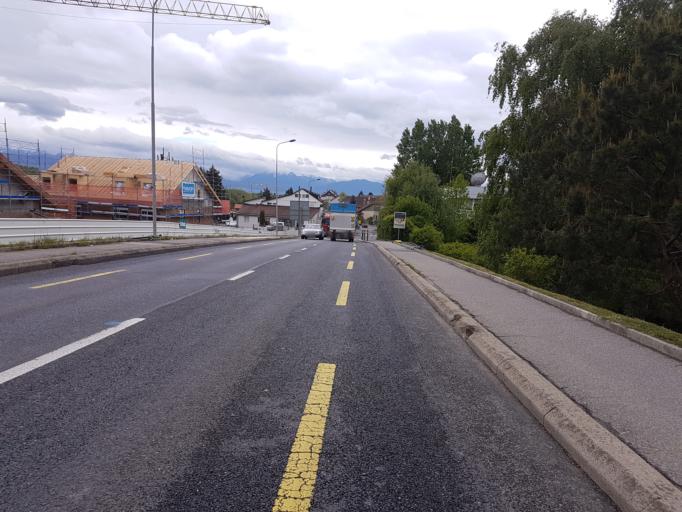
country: CH
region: Vaud
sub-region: Morges District
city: Preverenges
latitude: 46.5281
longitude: 6.5417
